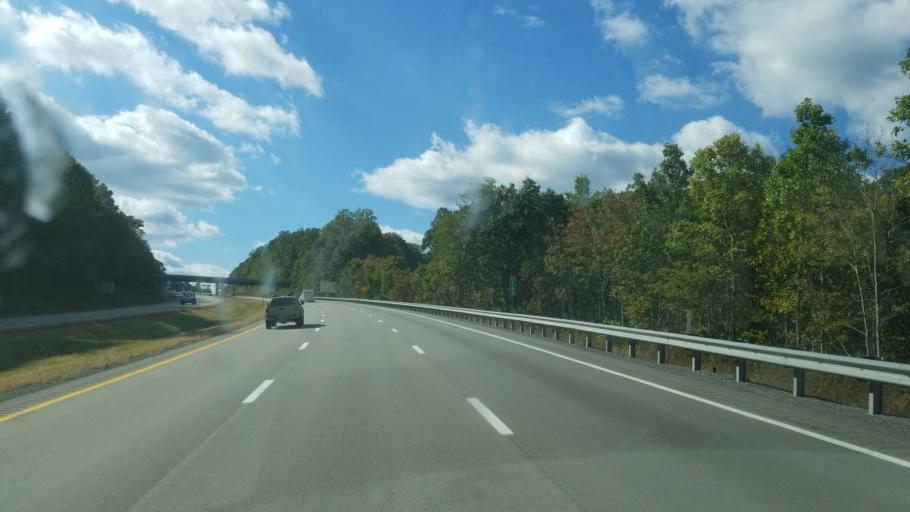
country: US
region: West Virginia
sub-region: Monongalia County
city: Cheat Lake
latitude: 39.6557
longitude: -79.7593
